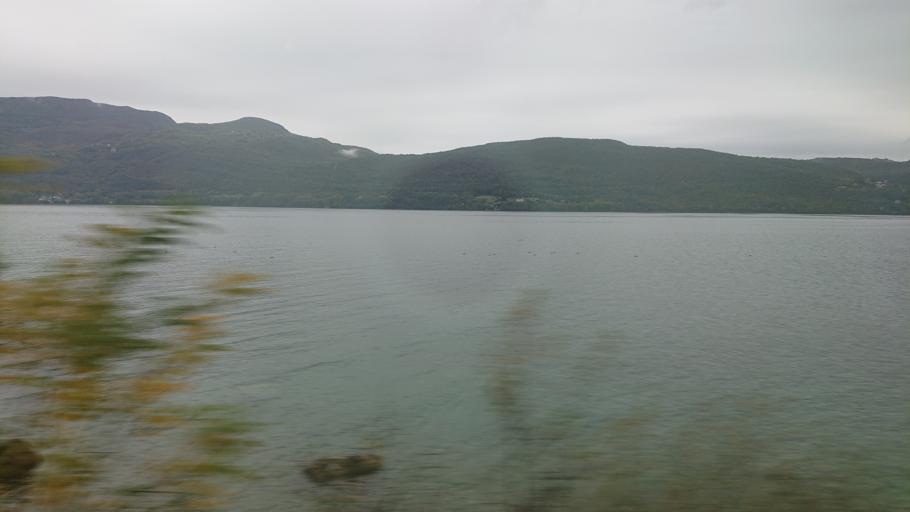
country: FR
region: Rhone-Alpes
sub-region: Departement de la Savoie
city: Chatillon
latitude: 45.7843
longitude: 5.8620
